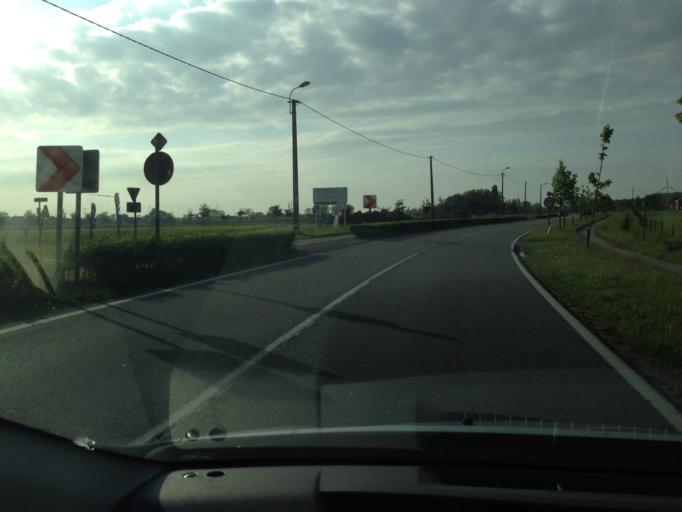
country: BE
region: Flanders
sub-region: Provincie West-Vlaanderen
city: Zedelgem
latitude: 51.1134
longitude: 3.1769
